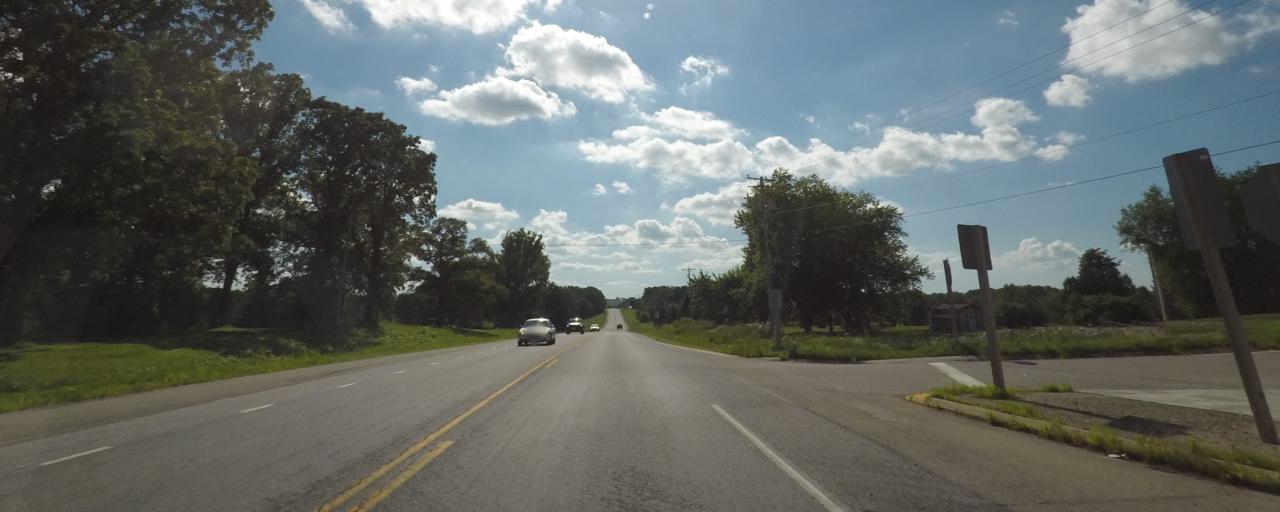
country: US
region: Wisconsin
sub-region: Rock County
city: Edgerton
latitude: 42.9205
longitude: -89.0989
